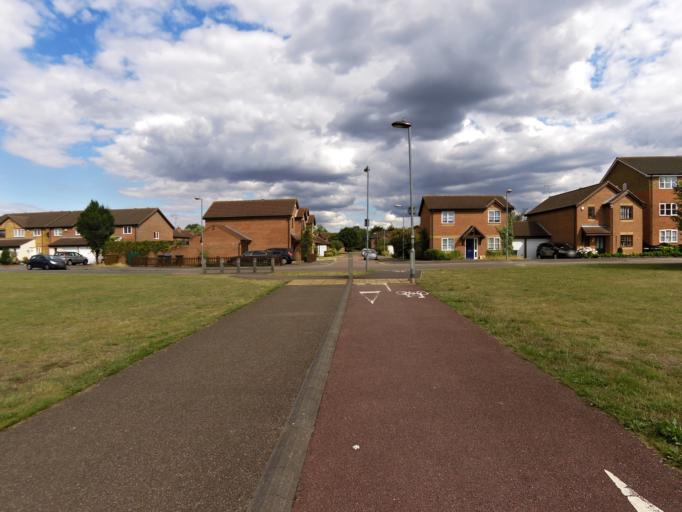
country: GB
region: England
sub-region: Essex
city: Waltham Abbey
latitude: 51.6670
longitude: -0.0138
